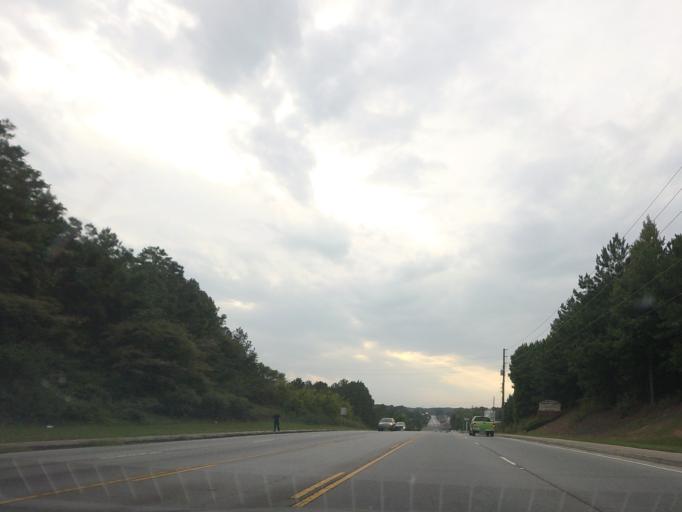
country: US
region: Georgia
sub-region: Bibb County
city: Macon
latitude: 32.8664
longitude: -83.6944
